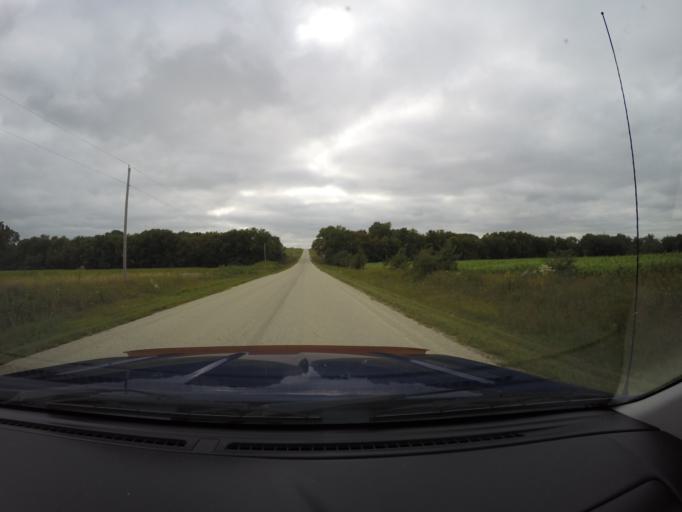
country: US
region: Kansas
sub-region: Dickinson County
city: Herington
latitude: 38.7973
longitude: -96.7851
